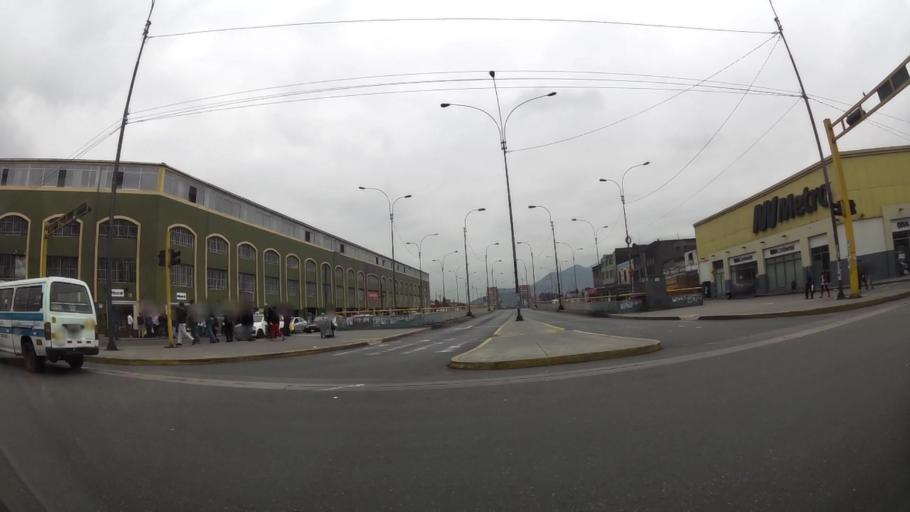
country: PE
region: Lima
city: Lima
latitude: -12.0430
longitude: -77.0431
